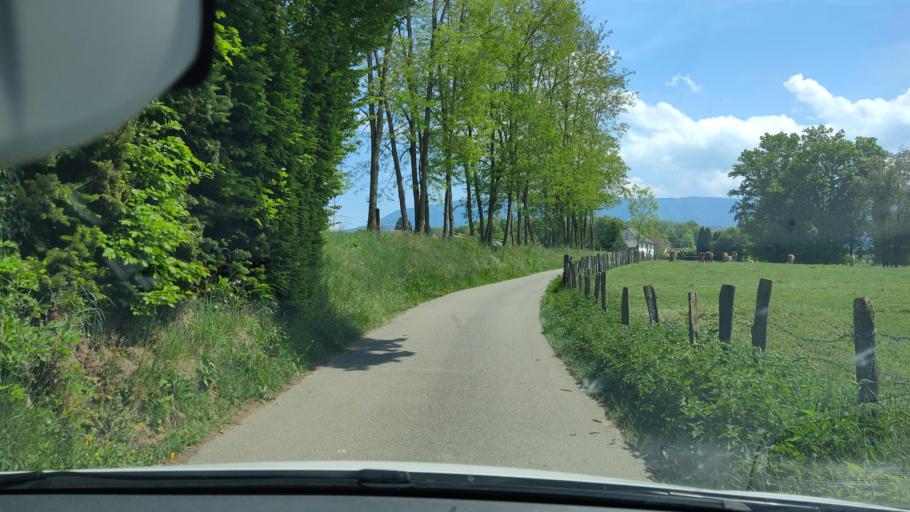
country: FR
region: Rhone-Alpes
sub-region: Departement de la Savoie
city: Domessin
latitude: 45.5290
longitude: 5.7088
